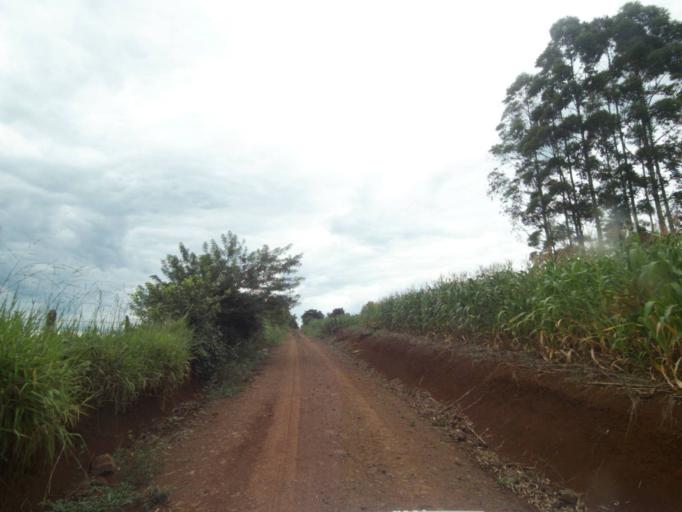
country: BR
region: Parana
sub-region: Guaraniacu
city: Guaraniacu
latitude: -24.9137
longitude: -52.9353
